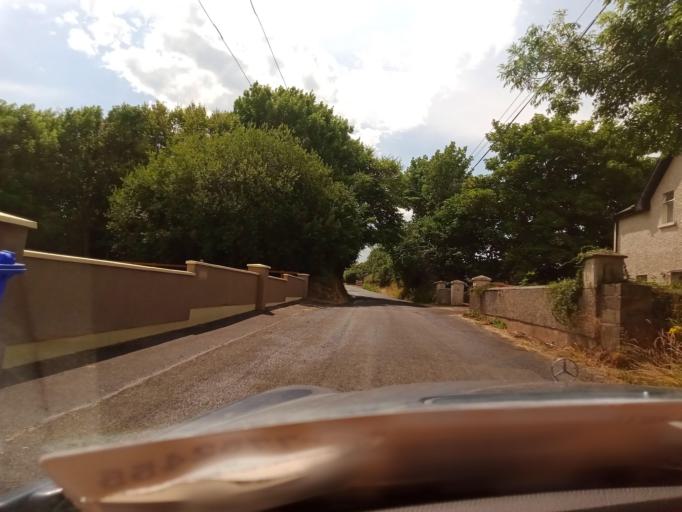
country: IE
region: Leinster
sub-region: Kilkenny
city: Mooncoin
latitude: 52.2743
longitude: -7.2173
